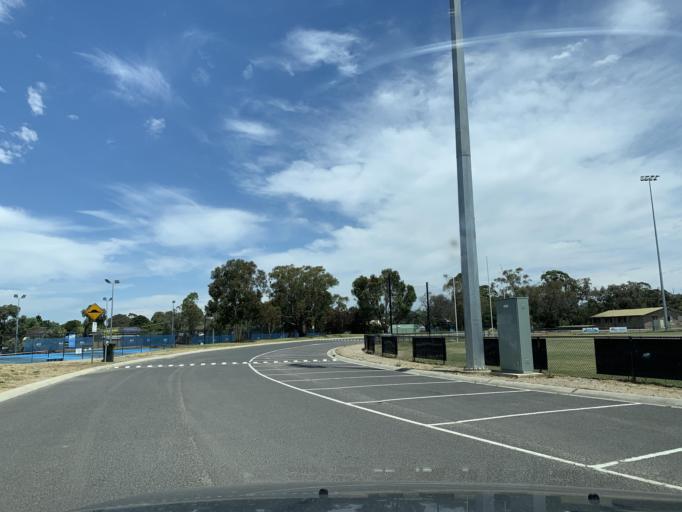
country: AU
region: Victoria
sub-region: Frankston
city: Langwarrin
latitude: -38.1492
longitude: 145.1903
